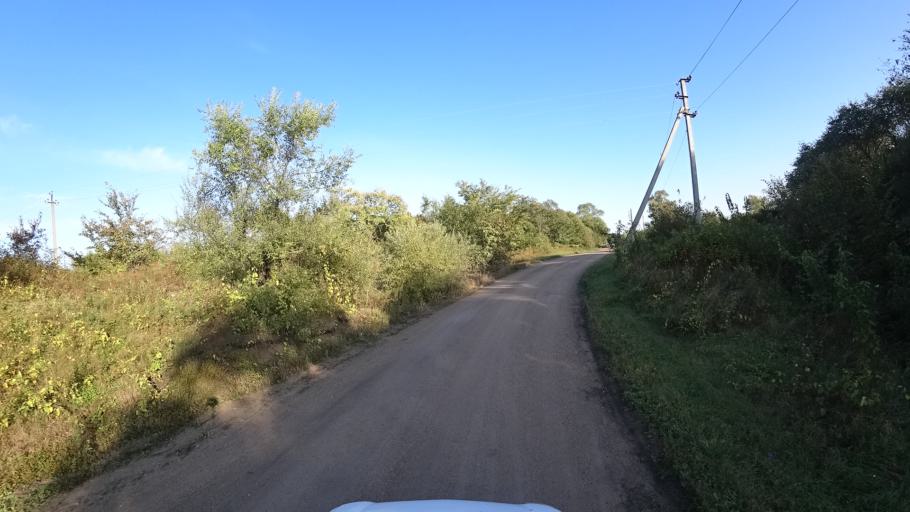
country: RU
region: Amur
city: Arkhara
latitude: 49.3625
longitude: 130.1234
